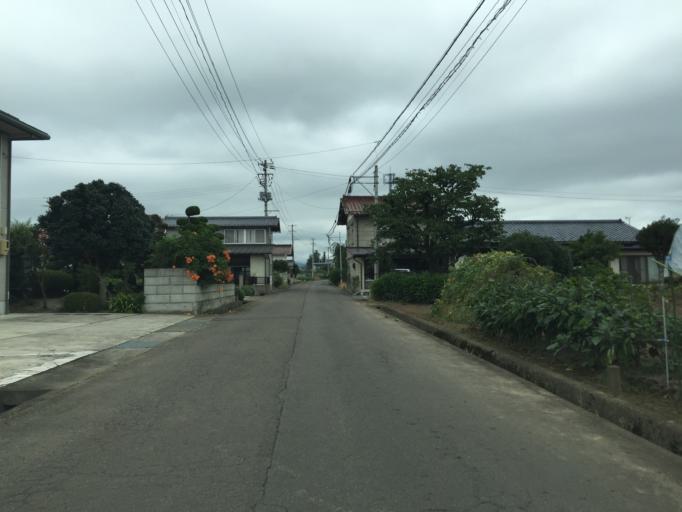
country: JP
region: Fukushima
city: Fukushima-shi
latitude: 37.7596
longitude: 140.4067
